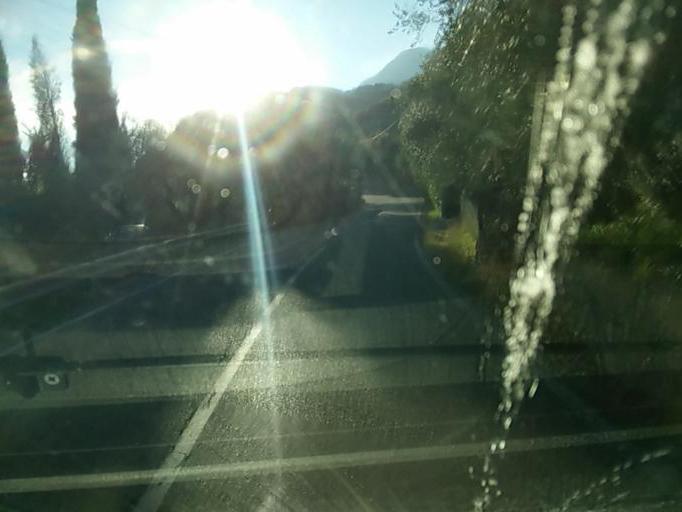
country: IT
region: Lombardy
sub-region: Provincia di Brescia
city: Gargnano
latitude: 45.6843
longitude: 10.6551
